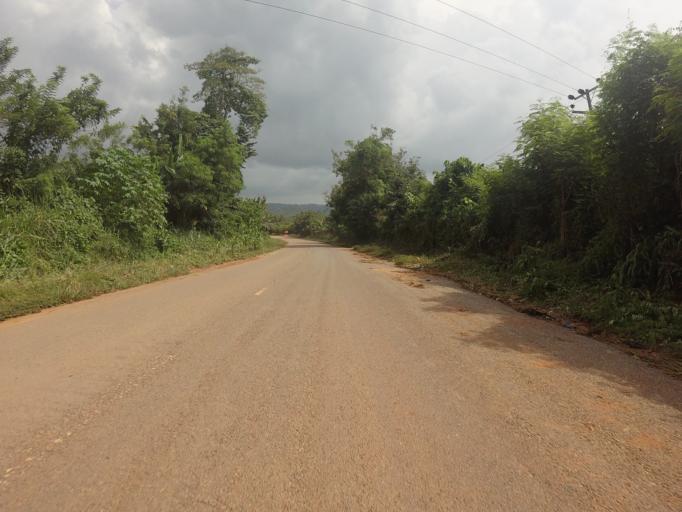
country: GH
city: Akropong
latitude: 5.9562
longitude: -0.1725
